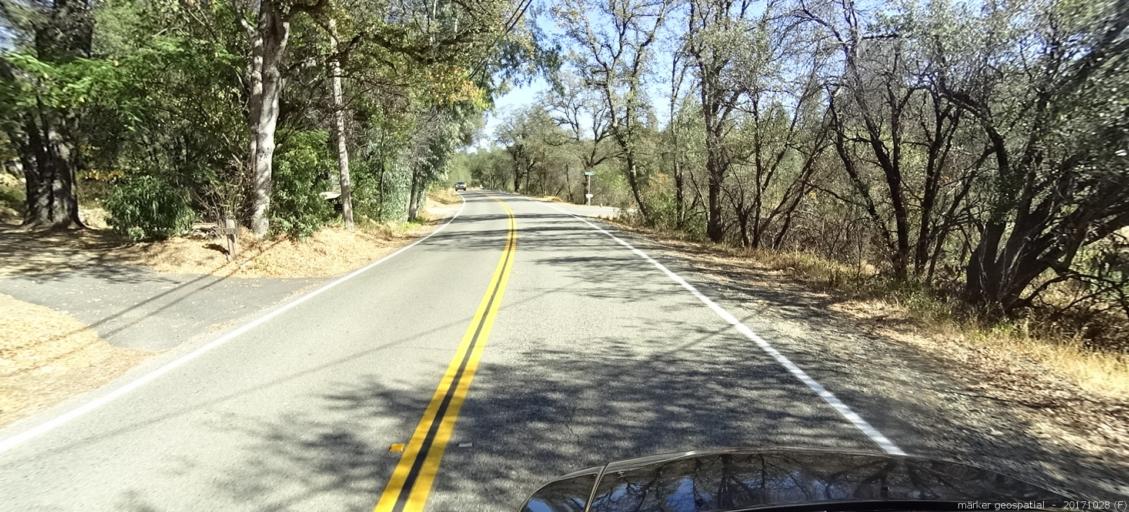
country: US
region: California
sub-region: Shasta County
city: Shasta
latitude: 40.6090
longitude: -122.4967
